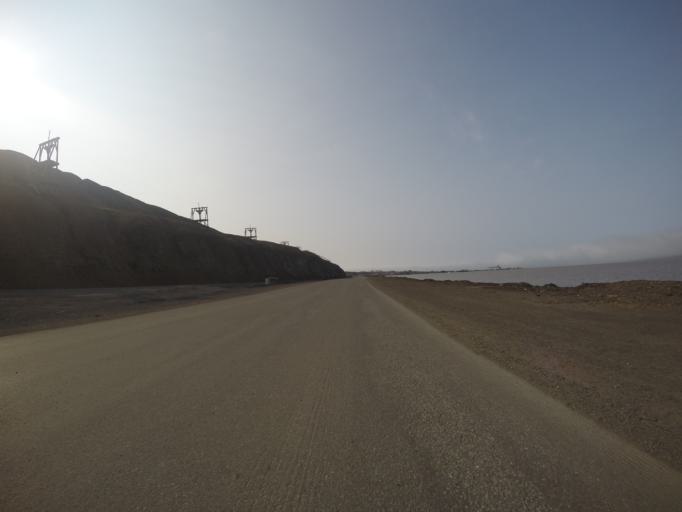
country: SJ
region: Svalbard
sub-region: Spitsbergen
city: Longyearbyen
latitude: 78.2321
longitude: 15.5704
